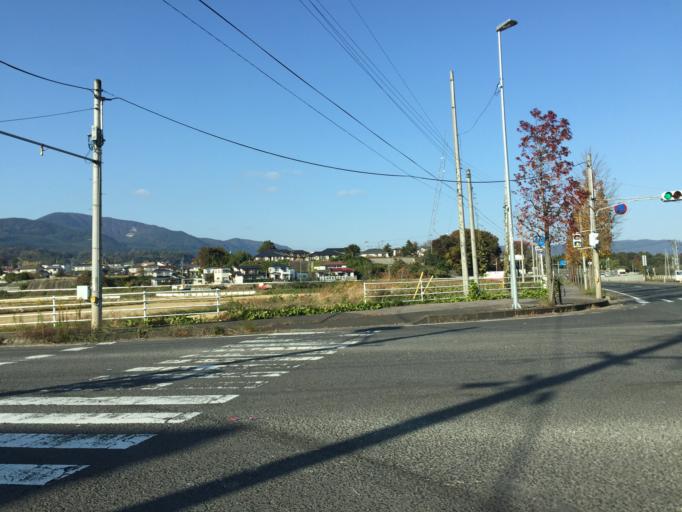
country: JP
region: Fukushima
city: Hobaramachi
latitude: 37.8369
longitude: 140.5196
